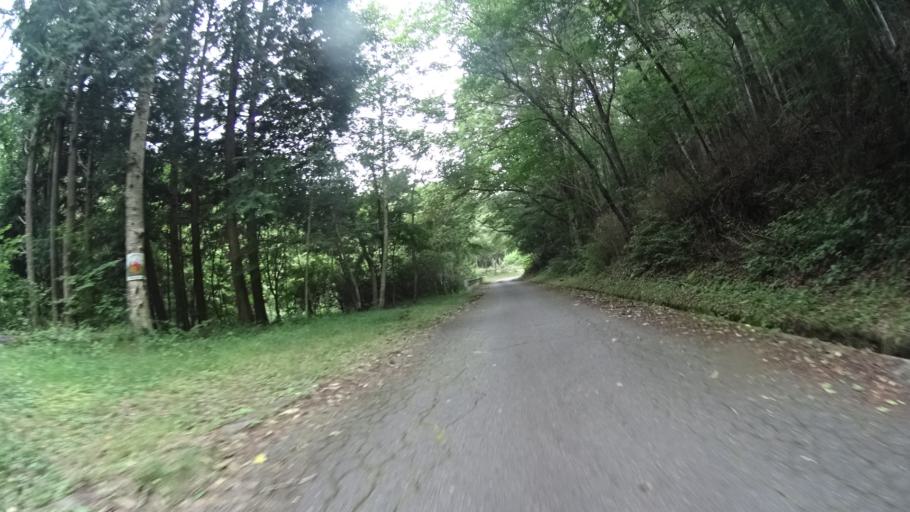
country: JP
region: Yamanashi
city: Kofu-shi
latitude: 35.8143
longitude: 138.5965
